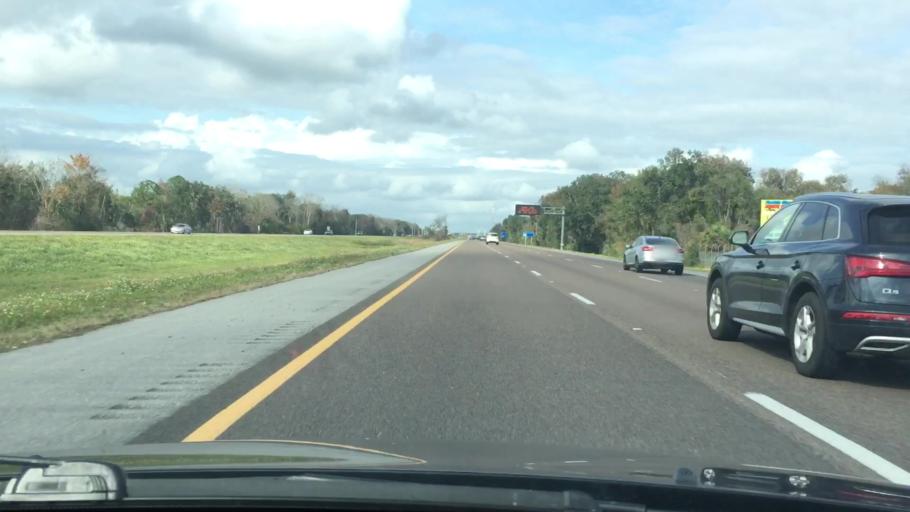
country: US
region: Florida
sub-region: Volusia County
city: Edgewater
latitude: 28.9364
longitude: -80.9438
